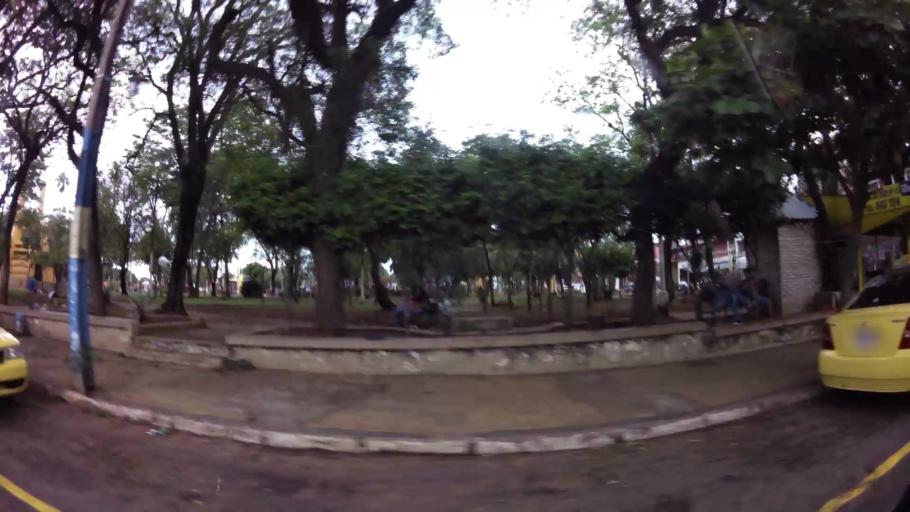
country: PY
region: Central
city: San Lorenzo
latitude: -25.2666
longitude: -57.4948
